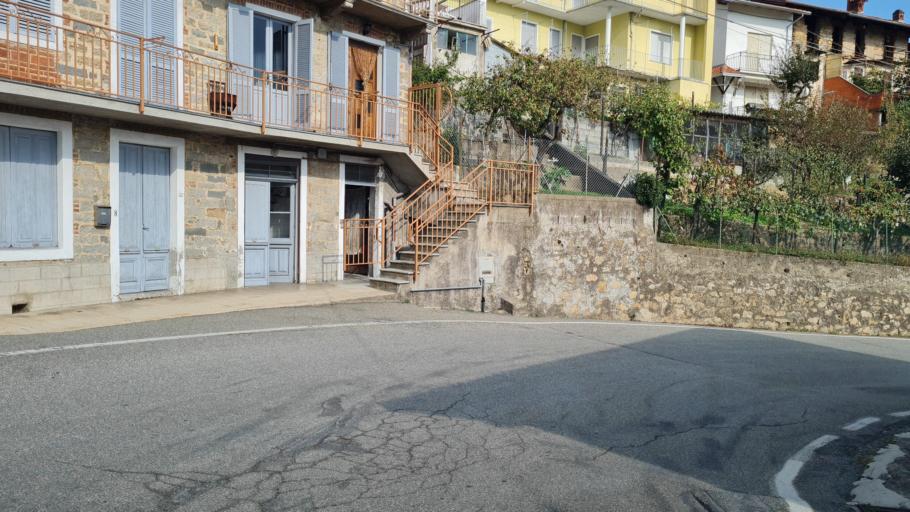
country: IT
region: Piedmont
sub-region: Provincia di Biella
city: Mezzana Mortigliengo
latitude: 45.6265
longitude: 8.1913
